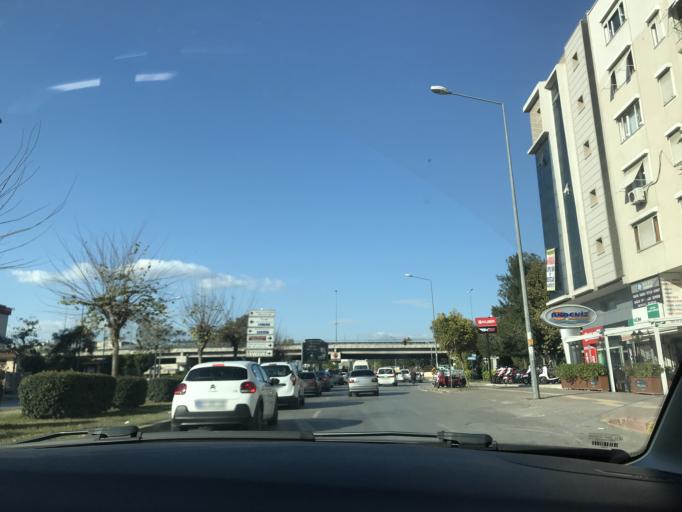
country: TR
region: Antalya
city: Antalya
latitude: 36.9097
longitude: 30.6985
